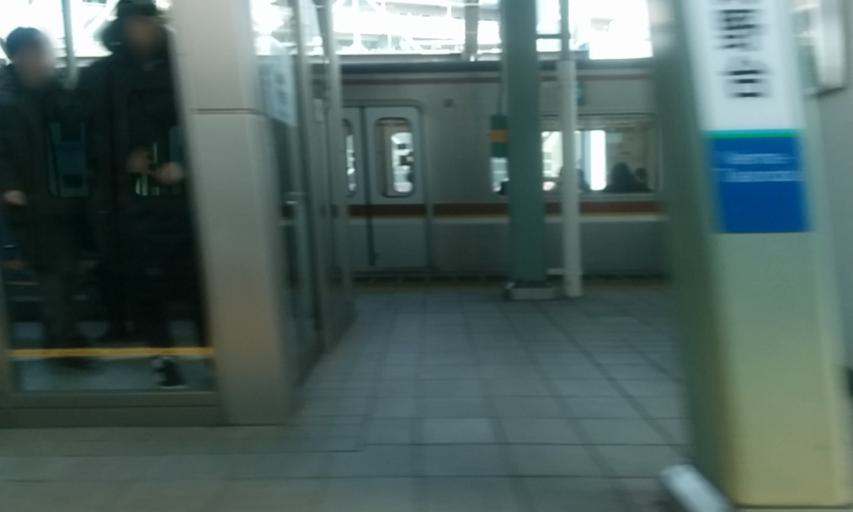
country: JP
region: Saitama
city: Wako
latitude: 35.7407
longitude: 139.6168
